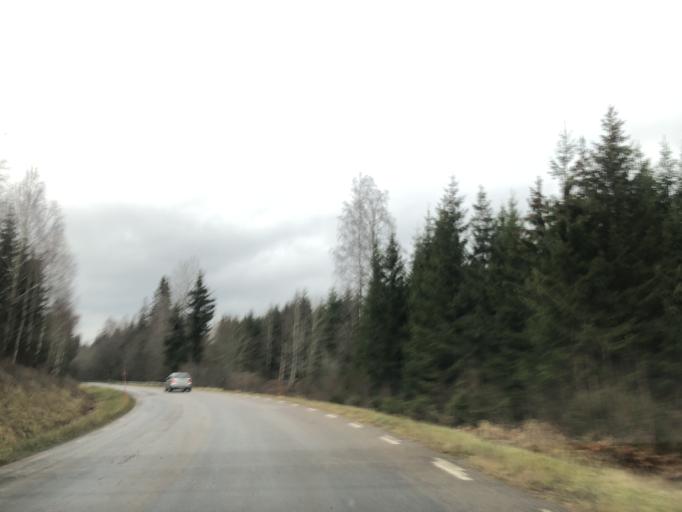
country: SE
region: Vaestra Goetaland
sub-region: Ulricehamns Kommun
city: Ulricehamn
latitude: 57.8999
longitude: 13.4871
